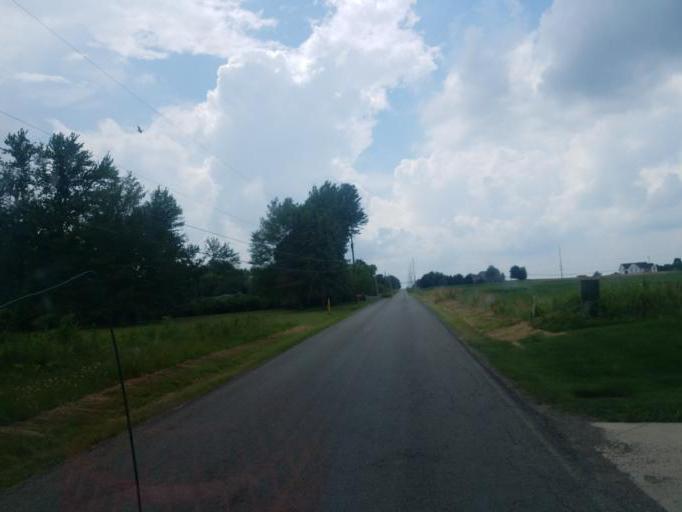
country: US
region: Ohio
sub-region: Mahoning County
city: Canfield
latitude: 40.9584
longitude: -80.7900
